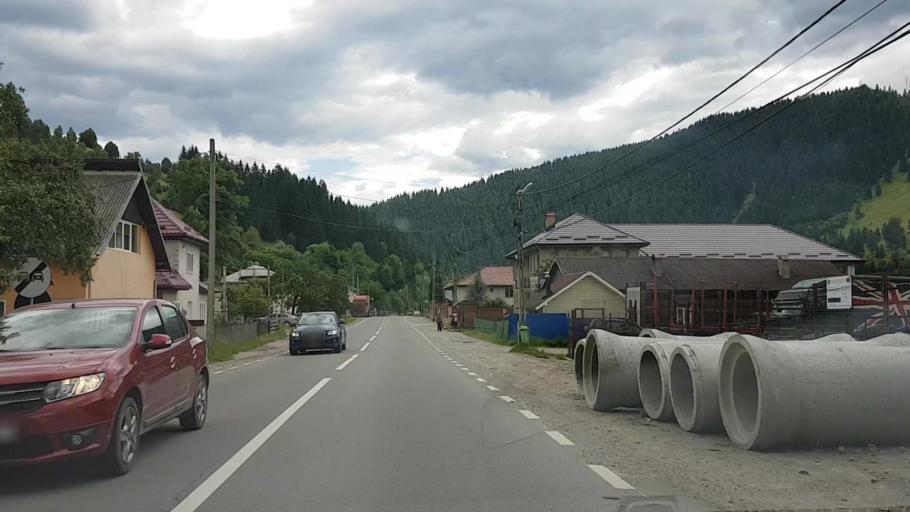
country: RO
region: Neamt
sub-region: Comuna Farcasa
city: Farcasa
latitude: 47.1557
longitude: 25.8400
